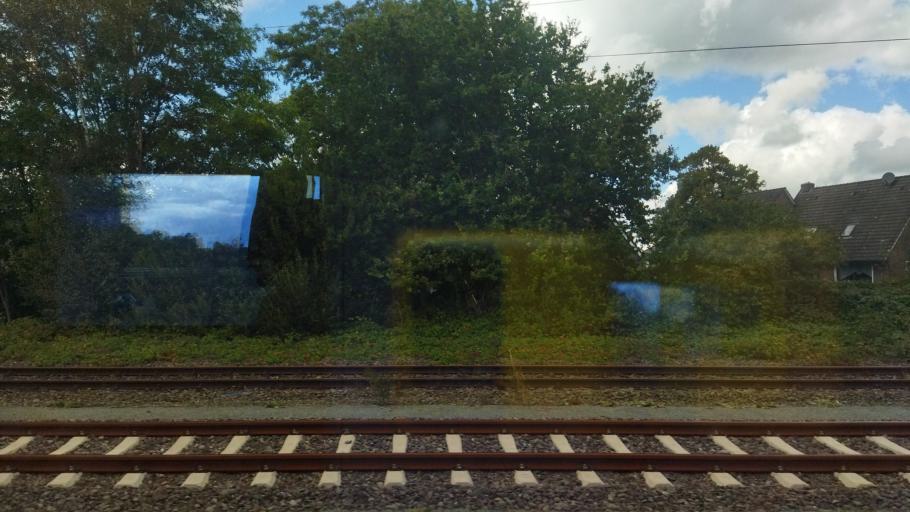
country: DE
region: Lower Saxony
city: Leer
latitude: 53.1605
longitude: 7.4440
